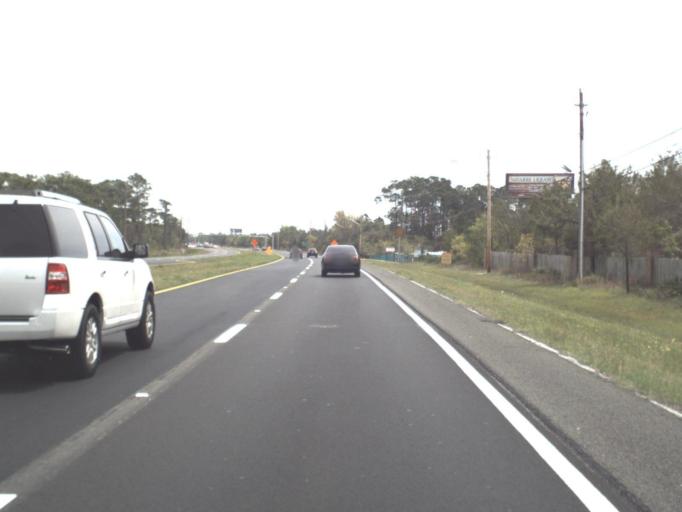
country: US
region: Florida
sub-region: Santa Rosa County
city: Woodlawn Beach
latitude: 30.4028
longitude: -86.9526
